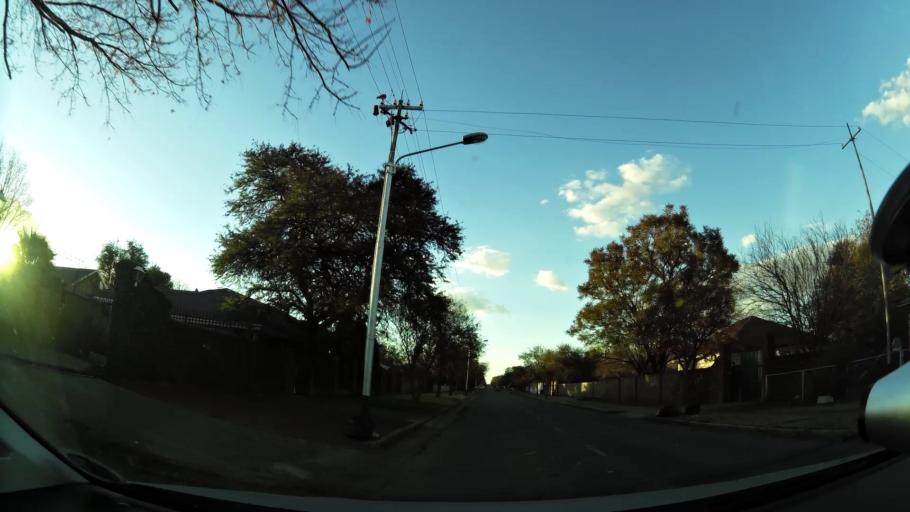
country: ZA
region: North-West
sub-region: Dr Kenneth Kaunda District Municipality
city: Potchefstroom
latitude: -26.7222
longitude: 27.0923
